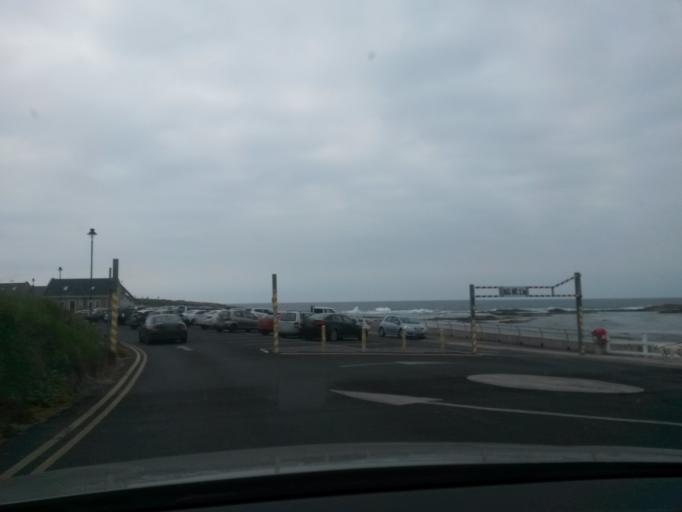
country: IE
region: Munster
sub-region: Ciarrai
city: Ballybunnion
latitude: 52.6818
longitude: -9.6631
